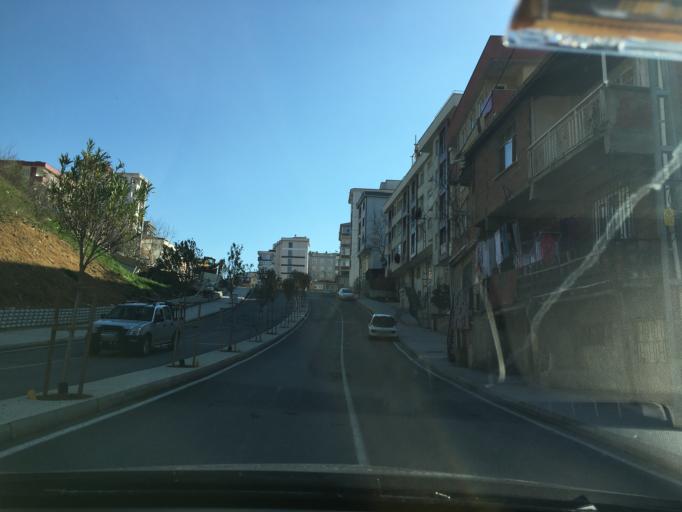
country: TR
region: Istanbul
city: Icmeler
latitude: 40.8706
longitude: 29.3021
